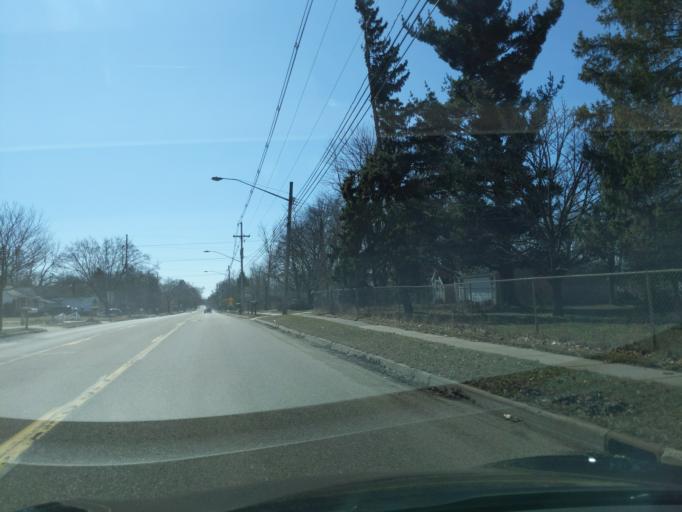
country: US
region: Michigan
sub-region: Ingham County
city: Lansing
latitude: 42.6804
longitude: -84.5629
